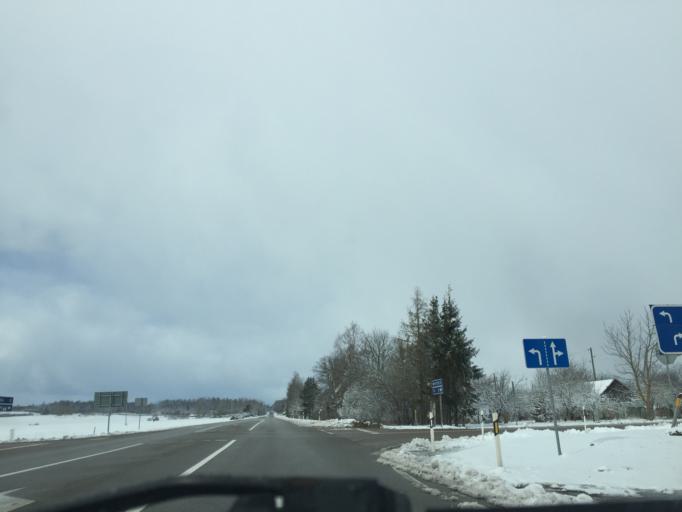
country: LV
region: Talsu Rajons
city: Talsi
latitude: 57.1707
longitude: 22.6589
